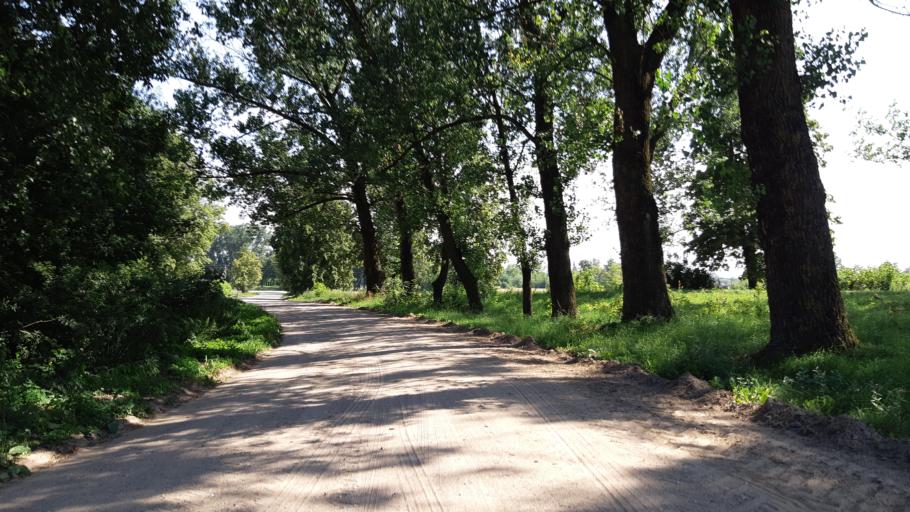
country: LT
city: Virbalis
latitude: 54.6353
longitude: 22.8253
